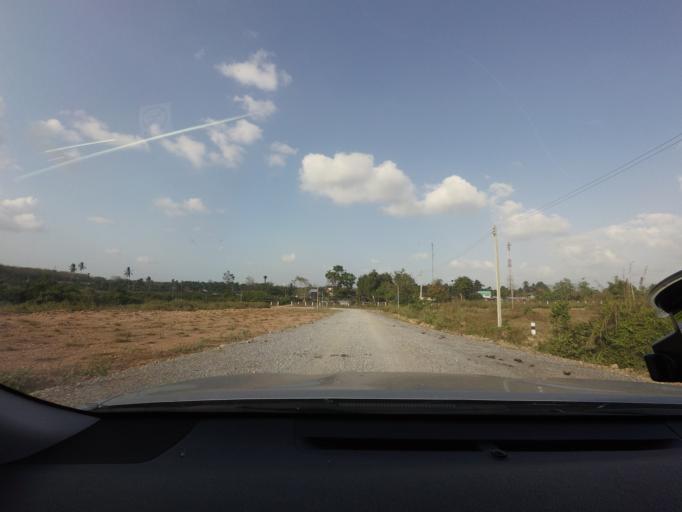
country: TH
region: Pattani
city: Mae Lan
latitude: 6.6136
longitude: 101.2572
